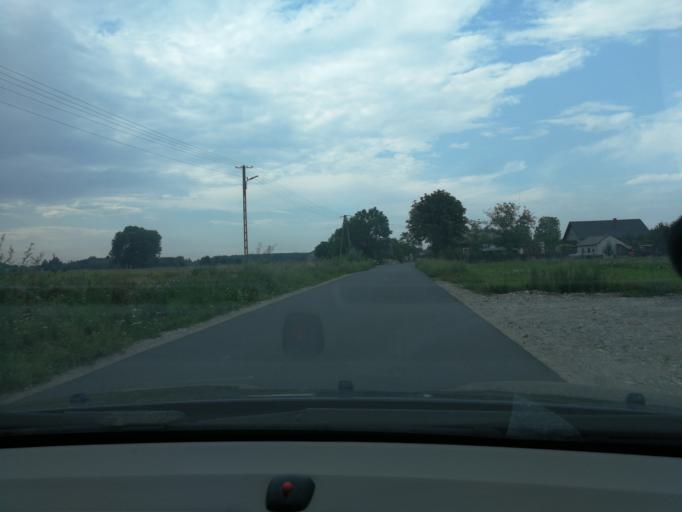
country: PL
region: Masovian Voivodeship
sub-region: Powiat warszawski zachodni
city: Bieniewice
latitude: 52.1051
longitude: 20.5554
